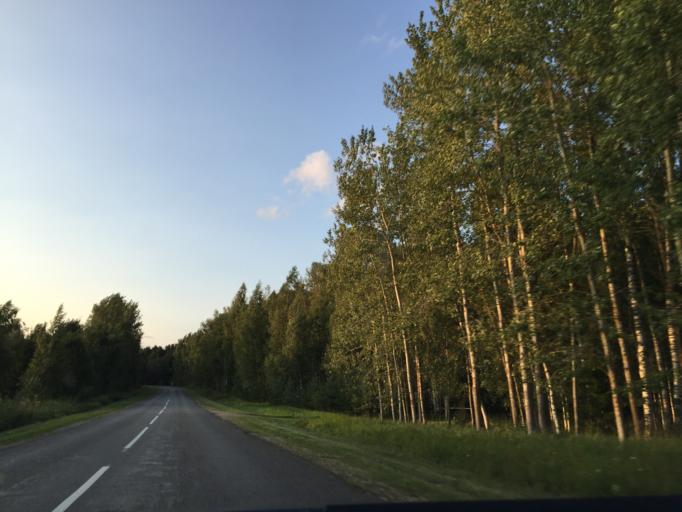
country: LV
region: Rezekne
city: Rezekne
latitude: 56.3454
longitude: 27.5112
